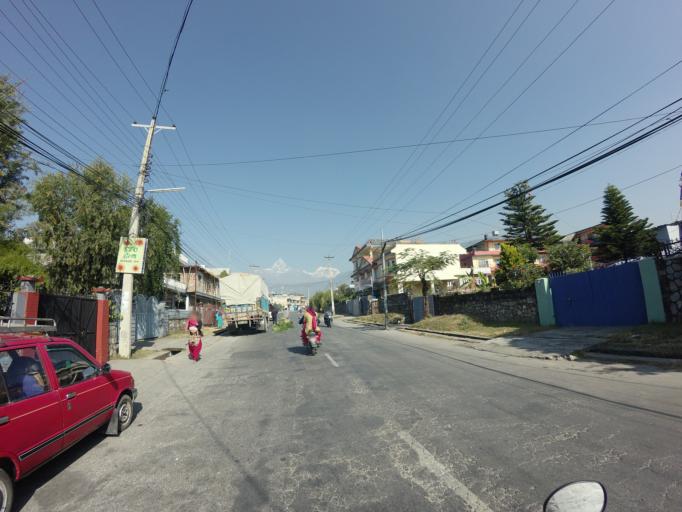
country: NP
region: Western Region
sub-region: Gandaki Zone
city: Pokhara
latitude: 28.2174
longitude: 83.9977
